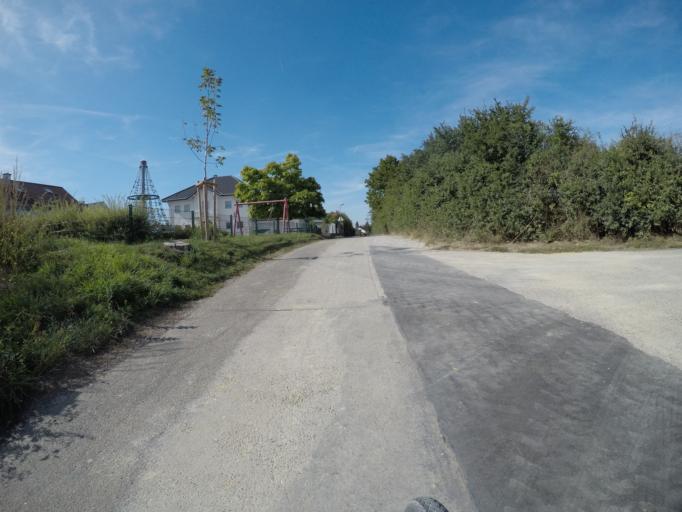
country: DE
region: Baden-Wuerttemberg
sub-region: Karlsruhe Region
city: Ubstadt-Weiher
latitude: 49.1578
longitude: 8.6398
